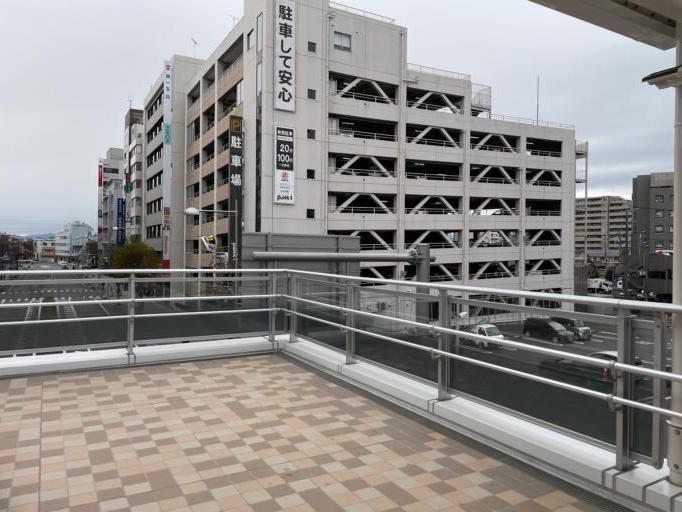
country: JP
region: Saitama
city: Kawagoe
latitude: 35.9064
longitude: 139.4814
